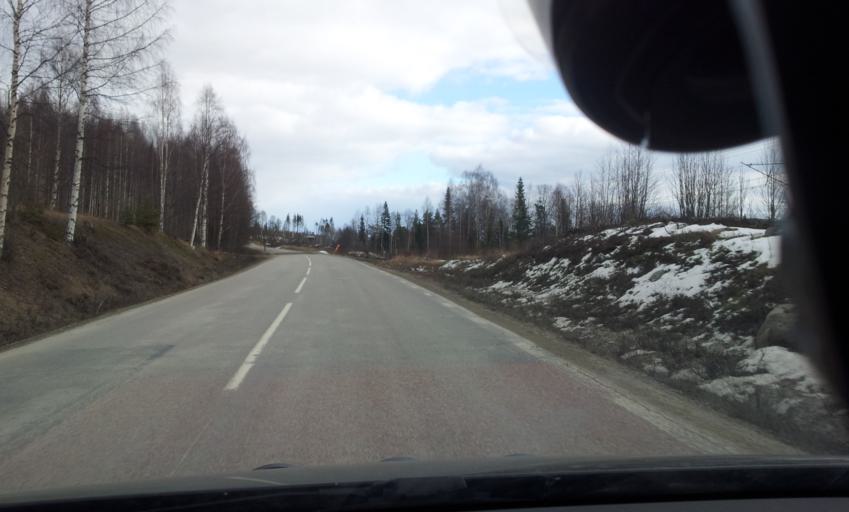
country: SE
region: Gaevleborg
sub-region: Ljusdals Kommun
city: Farila
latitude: 62.1318
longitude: 15.6982
